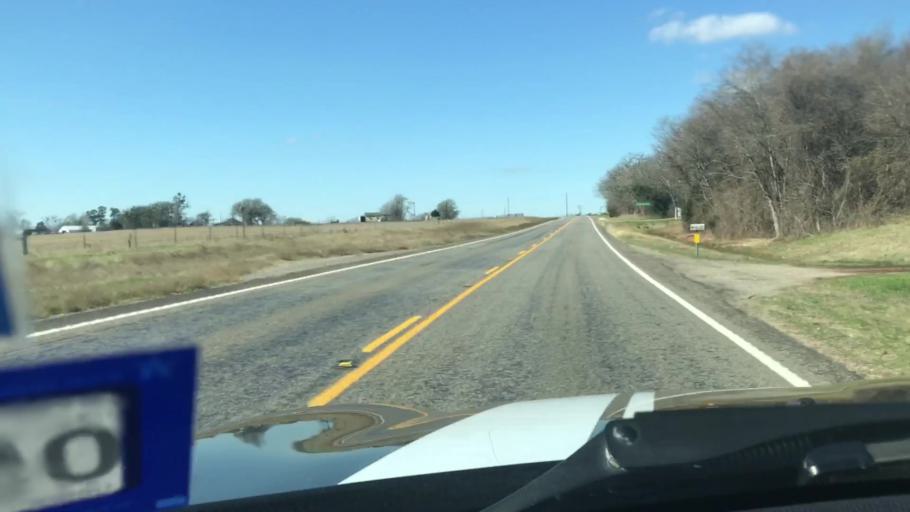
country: US
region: Texas
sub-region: Robertson County
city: Calvert
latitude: 30.8834
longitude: -96.7487
